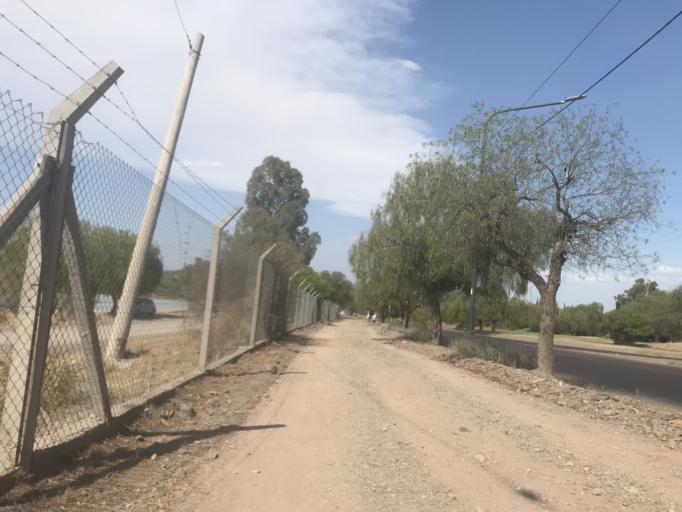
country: AR
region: Mendoza
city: Mendoza
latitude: -32.8826
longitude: -68.8866
